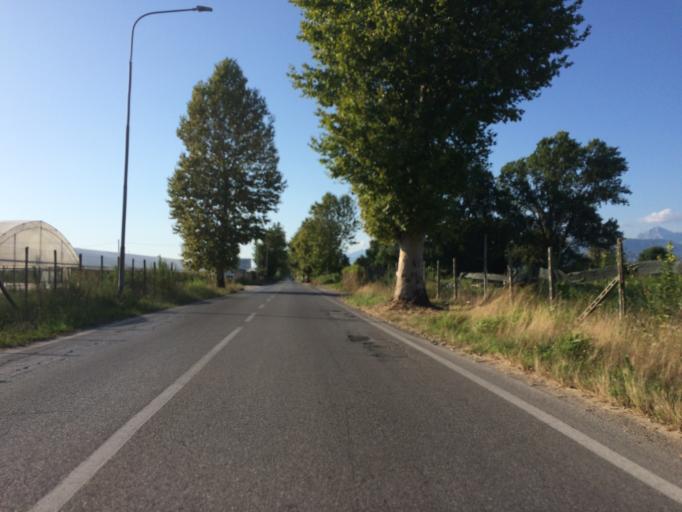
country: IT
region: Tuscany
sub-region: Provincia di Lucca
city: Torre del Lago Puccini
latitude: 43.8393
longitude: 10.2846
